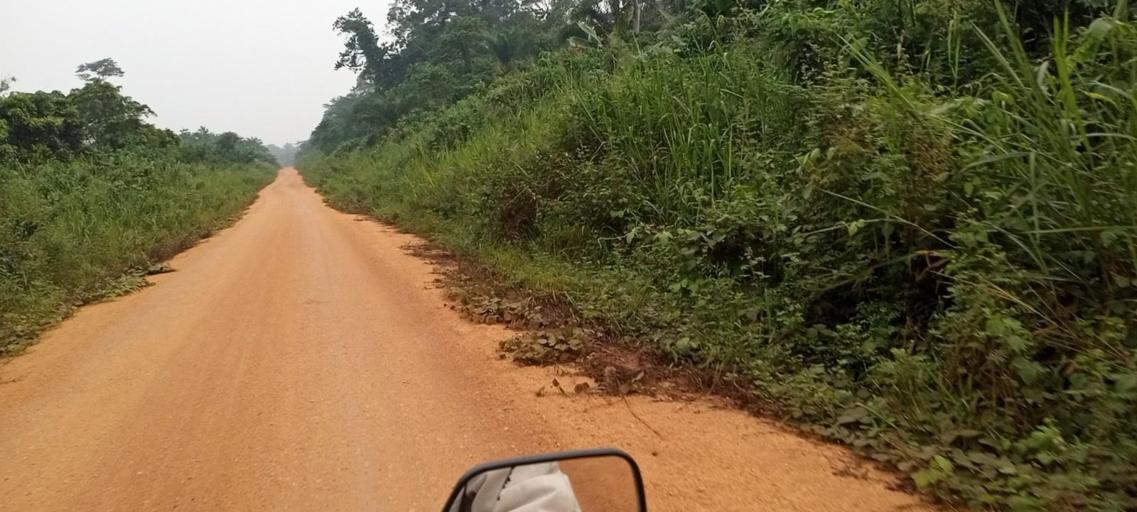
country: CD
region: Eastern Province
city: Kisangani
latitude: 0.0474
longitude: 25.5532
